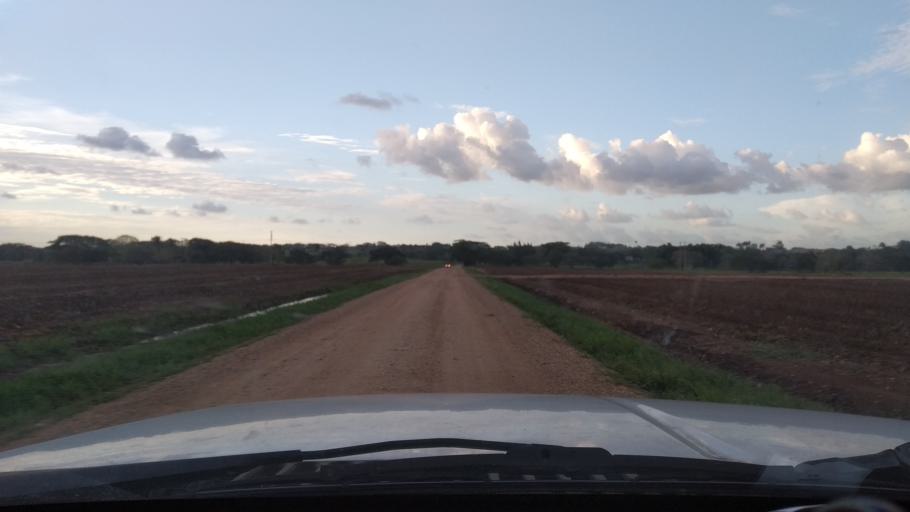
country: BZ
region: Cayo
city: San Ignacio
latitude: 17.2176
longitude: -88.9984
